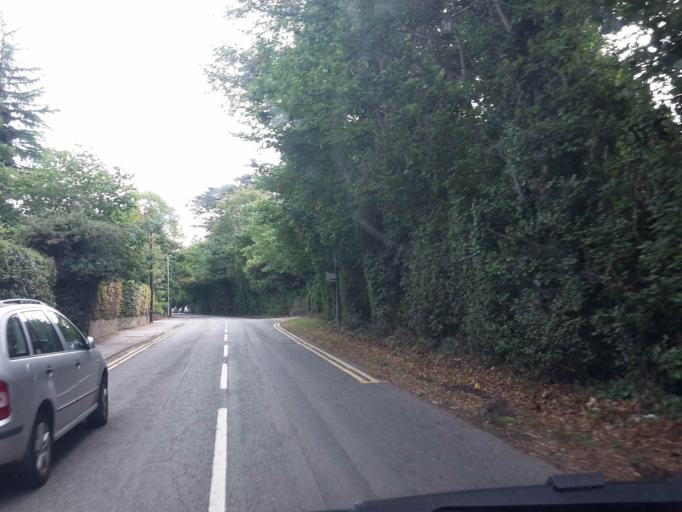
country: GB
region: England
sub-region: Wokingham
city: Wokingham
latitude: 51.4172
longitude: -0.8298
